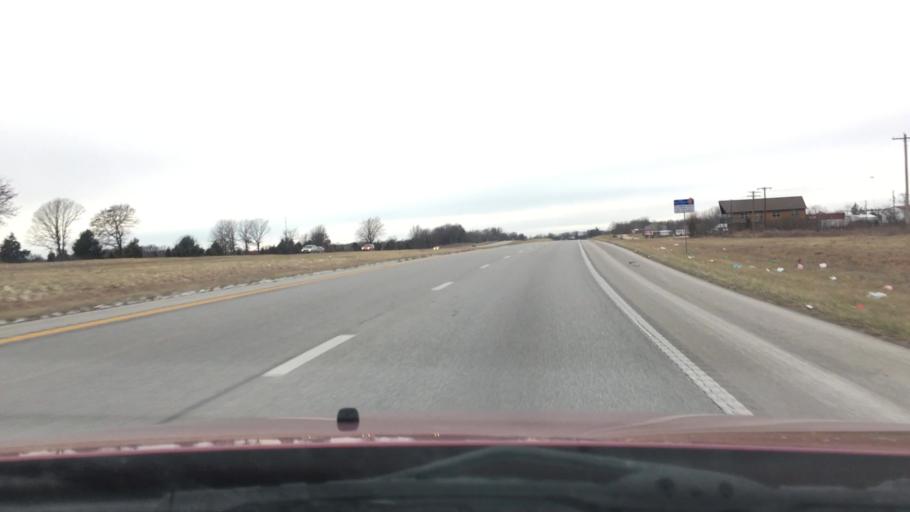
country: US
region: Missouri
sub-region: Webster County
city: Seymour
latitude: 37.1583
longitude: -92.7897
